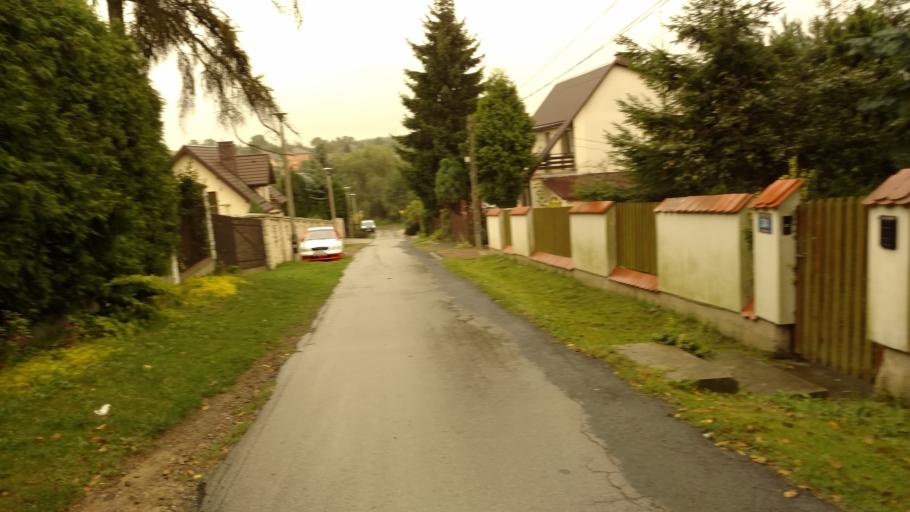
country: PL
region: Lesser Poland Voivodeship
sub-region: Powiat krakowski
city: Michalowice
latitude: 50.1334
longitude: 19.9708
